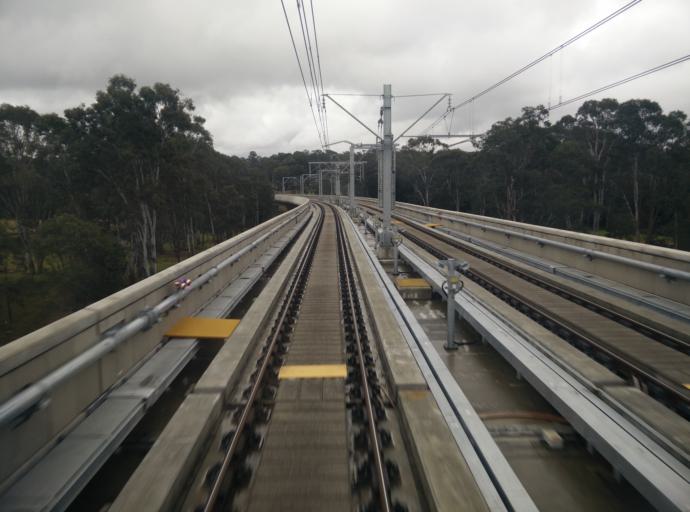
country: AU
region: New South Wales
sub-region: Blacktown
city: Rouse Hill
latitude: -33.6903
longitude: 150.9122
